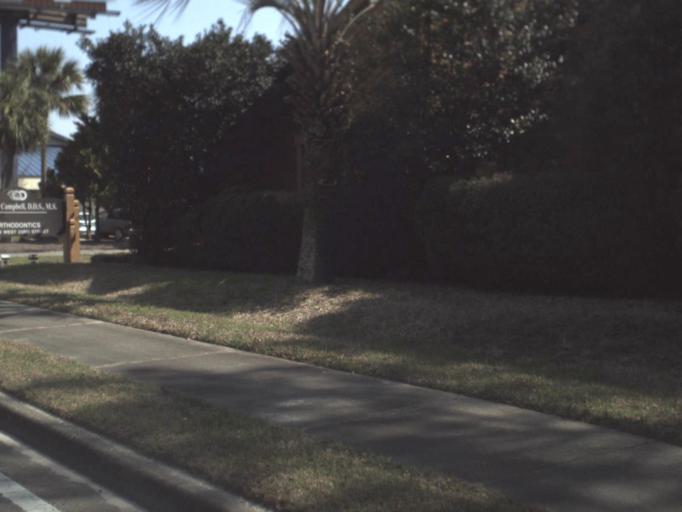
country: US
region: Florida
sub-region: Bay County
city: Panama City
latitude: 30.1895
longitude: -85.6596
